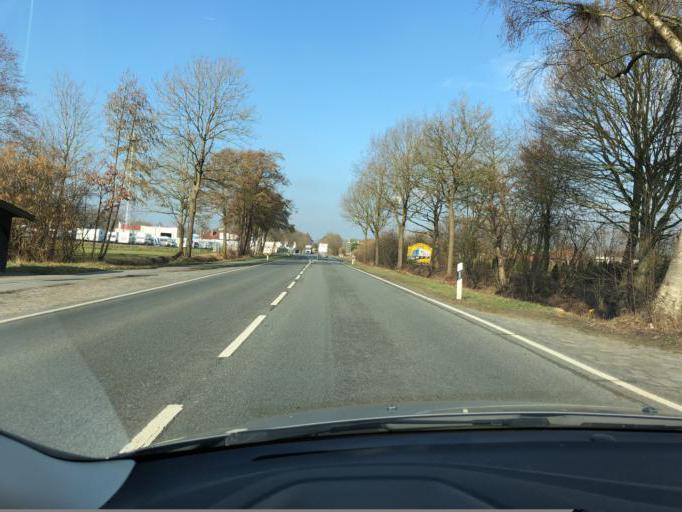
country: DE
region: Lower Saxony
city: Westerstede
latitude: 53.2860
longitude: 7.8957
